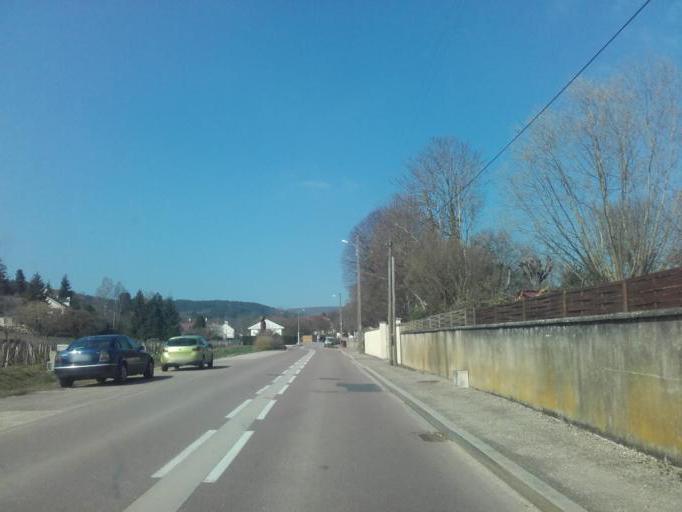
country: FR
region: Bourgogne
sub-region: Departement de la Cote-d'Or
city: Savigny-les-Beaune
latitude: 47.0593
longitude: 4.8274
